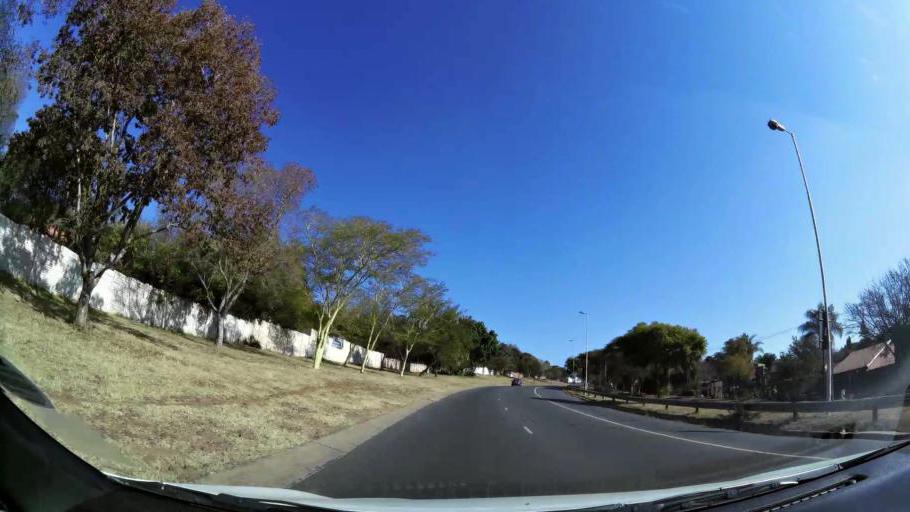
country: ZA
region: Gauteng
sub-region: City of Tshwane Metropolitan Municipality
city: Centurion
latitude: -25.8090
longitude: 28.2813
